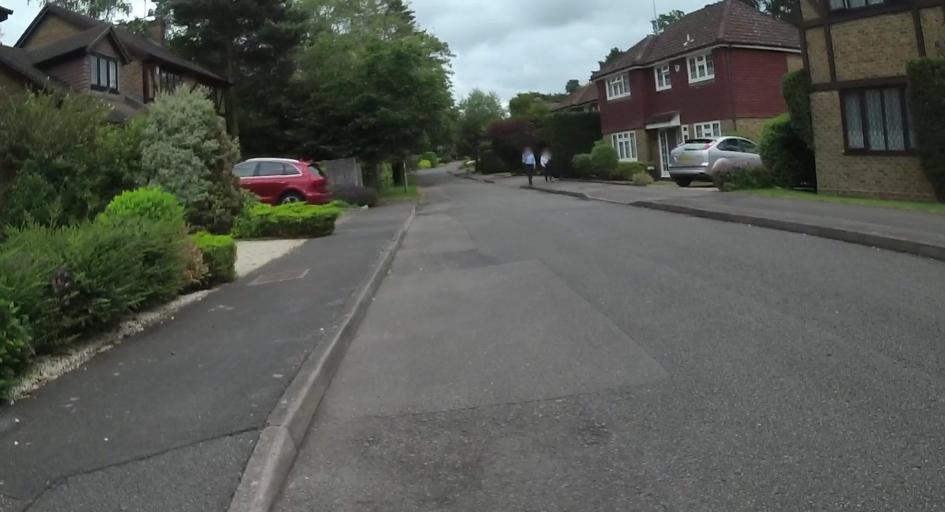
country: GB
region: England
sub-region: Bracknell Forest
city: Crowthorne
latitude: 51.3675
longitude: -0.7986
